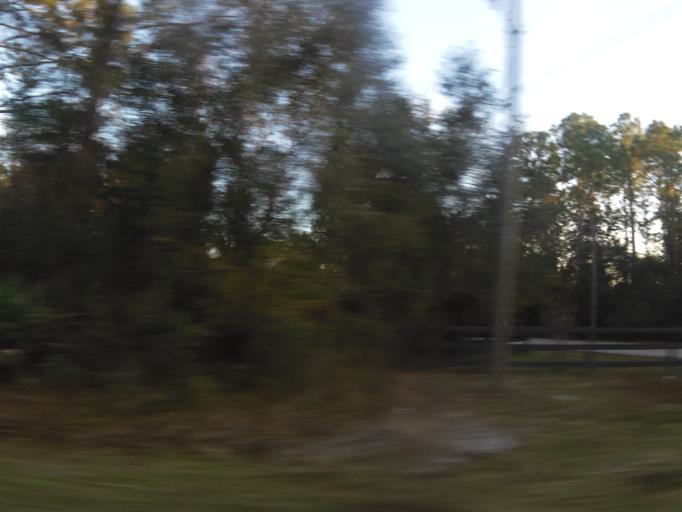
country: US
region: Florida
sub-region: Clay County
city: Green Cove Springs
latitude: 29.9384
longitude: -81.5656
